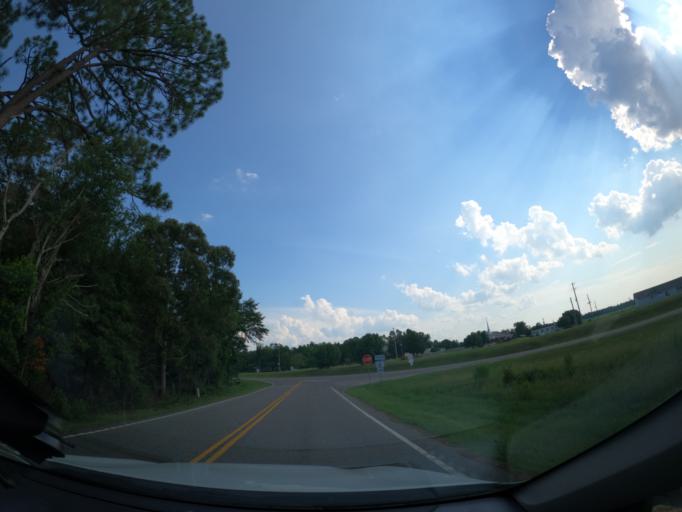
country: US
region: South Carolina
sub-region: Barnwell County
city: Williston
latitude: 33.4846
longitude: -81.5163
